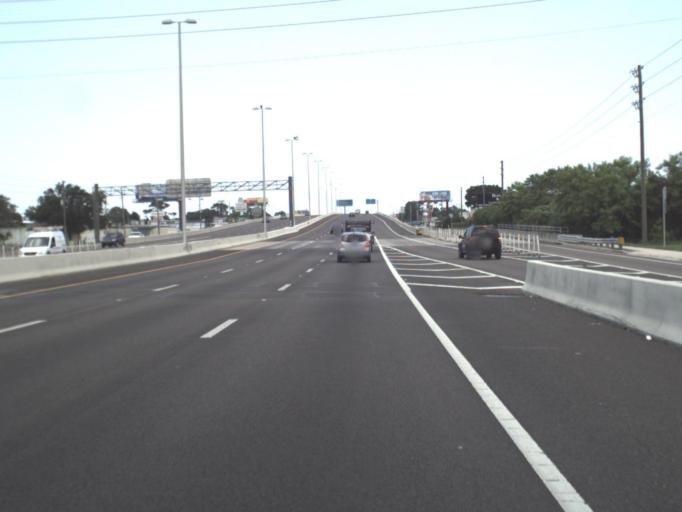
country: US
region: Florida
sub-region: Pinellas County
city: South Highpoint
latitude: 27.8822
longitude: -82.7142
